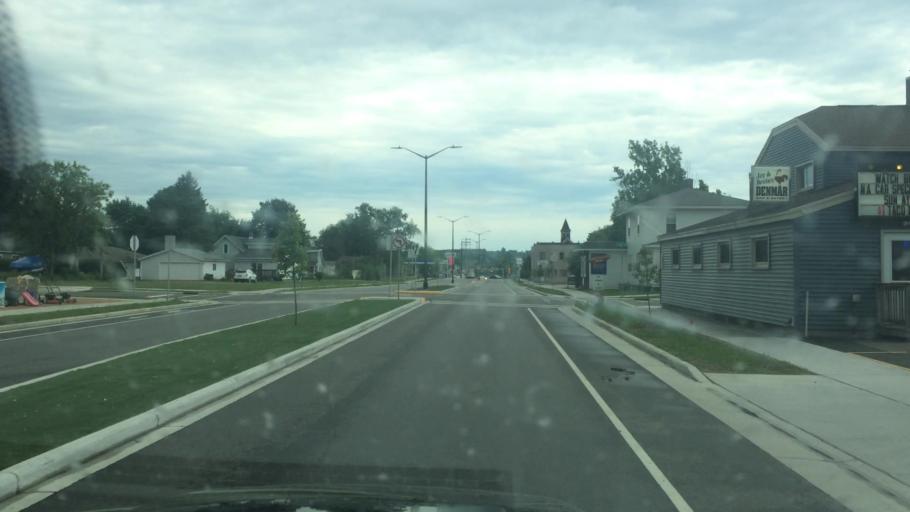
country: US
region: Wisconsin
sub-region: Marathon County
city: Wausau
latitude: 44.9483
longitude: -89.6436
